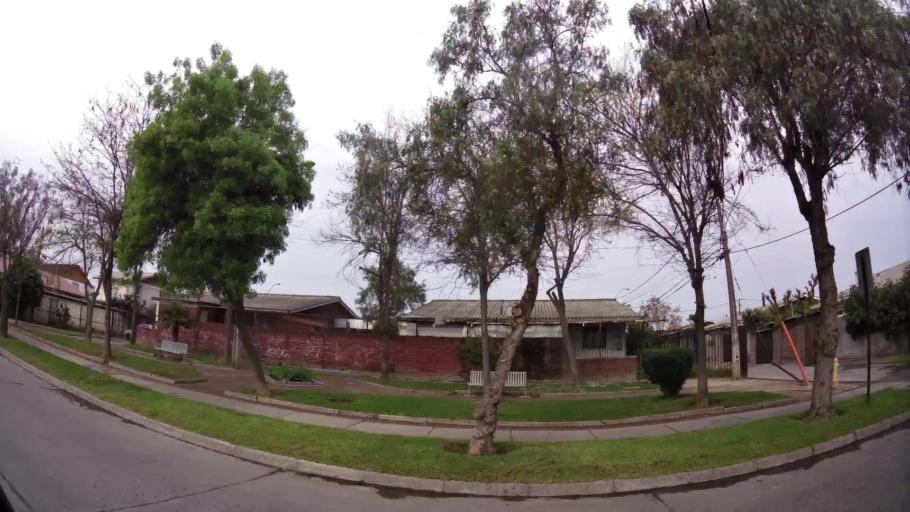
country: CL
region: Santiago Metropolitan
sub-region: Provincia de Santiago
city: Lo Prado
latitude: -33.5222
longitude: -70.7723
